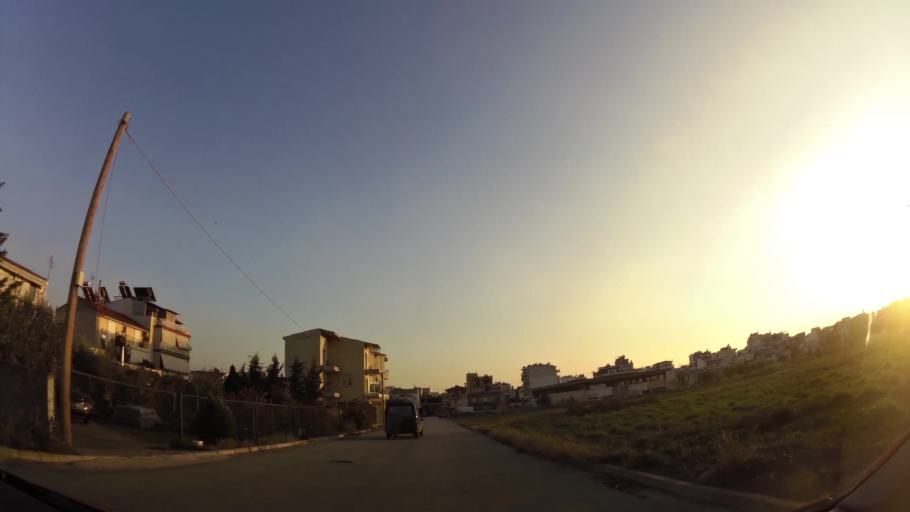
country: GR
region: Attica
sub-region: Nomarchia Anatolikis Attikis
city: Acharnes
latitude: 38.0914
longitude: 23.7413
